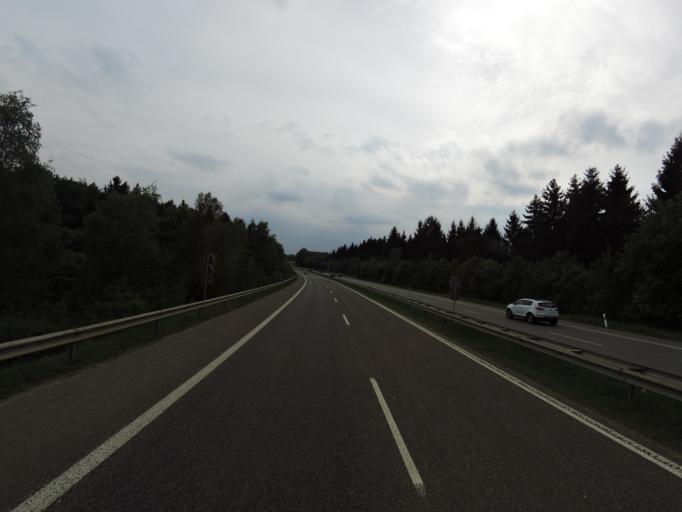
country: DE
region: Rheinland-Pfalz
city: Waldesch
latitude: 50.2525
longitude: 7.5220
